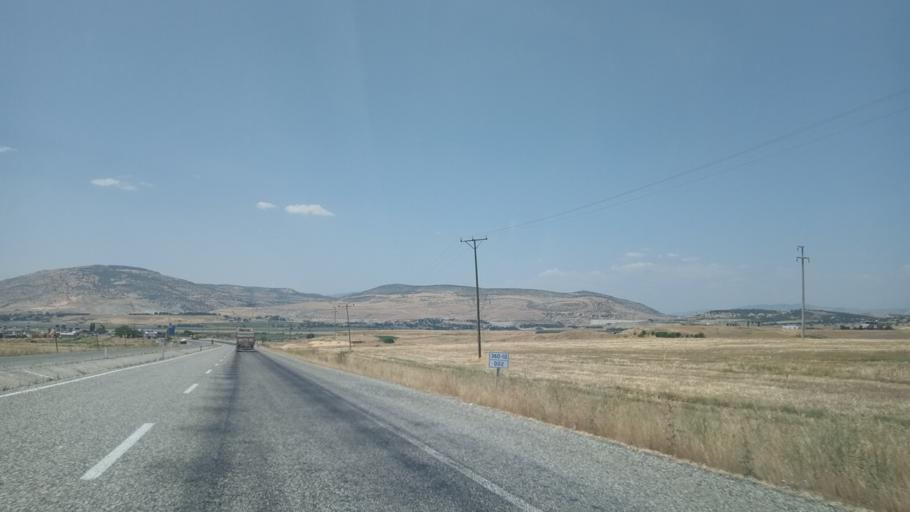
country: TR
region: Diyarbakir
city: Malabadi
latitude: 38.1345
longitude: 41.2390
